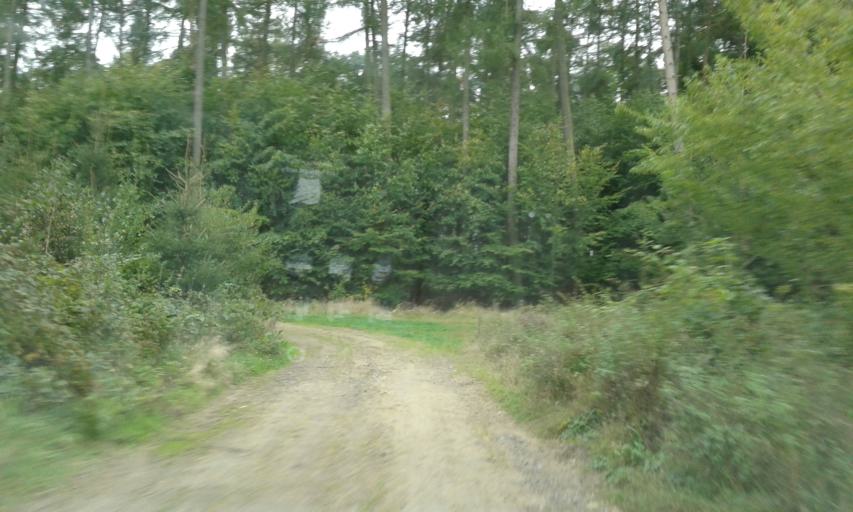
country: PL
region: West Pomeranian Voivodeship
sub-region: Powiat choszczenski
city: Pelczyce
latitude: 53.0851
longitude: 15.2525
